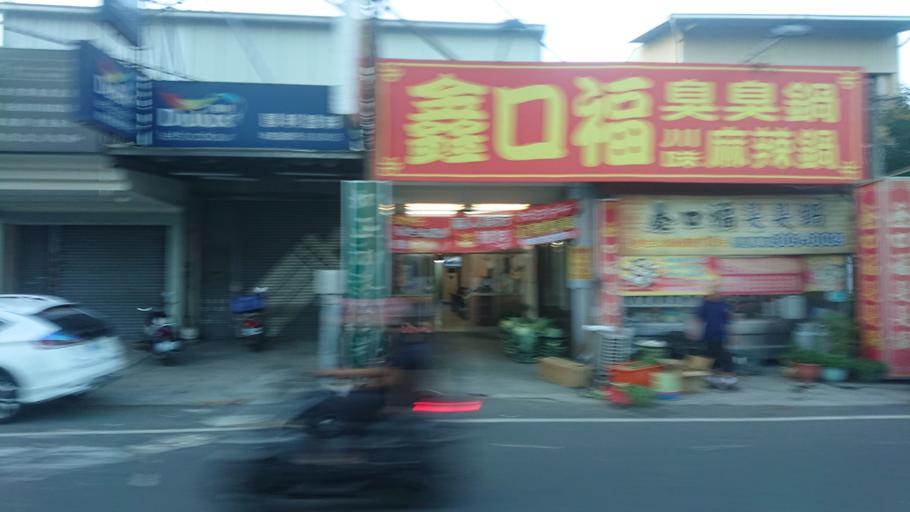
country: TW
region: Taiwan
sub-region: Tainan
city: Tainan
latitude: 23.0166
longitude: 120.2372
